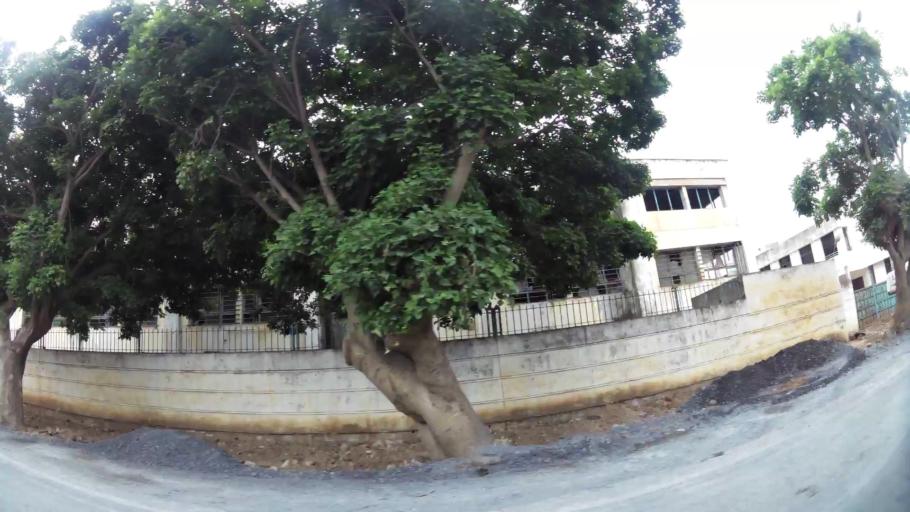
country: MA
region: Rabat-Sale-Zemmour-Zaer
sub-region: Rabat
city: Rabat
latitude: 33.9881
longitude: -6.8035
